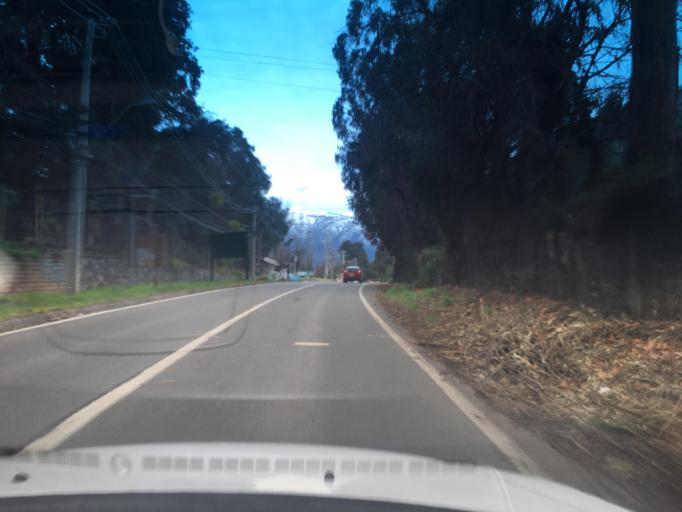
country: CL
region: Santiago Metropolitan
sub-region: Provincia de Cordillera
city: Puente Alto
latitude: -33.5773
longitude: -70.4361
